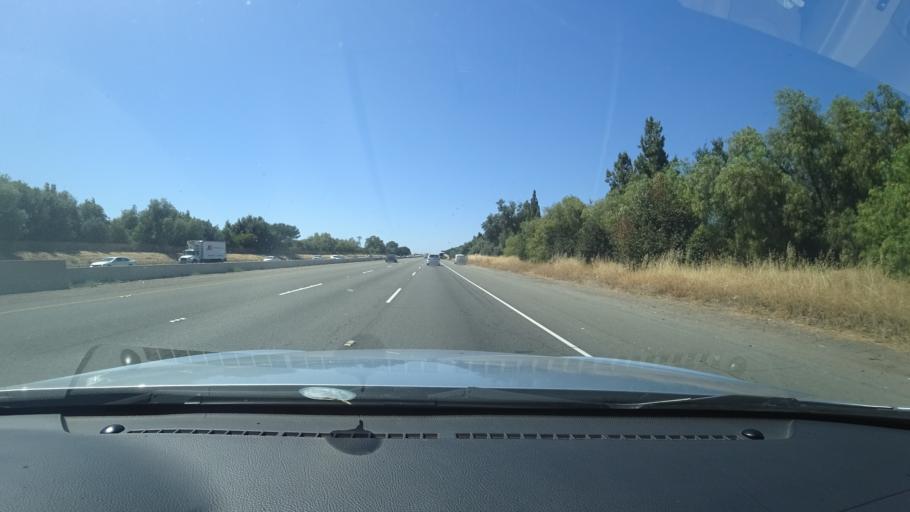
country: US
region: California
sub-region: Santa Clara County
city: Milpitas
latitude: 37.4589
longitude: -121.8991
